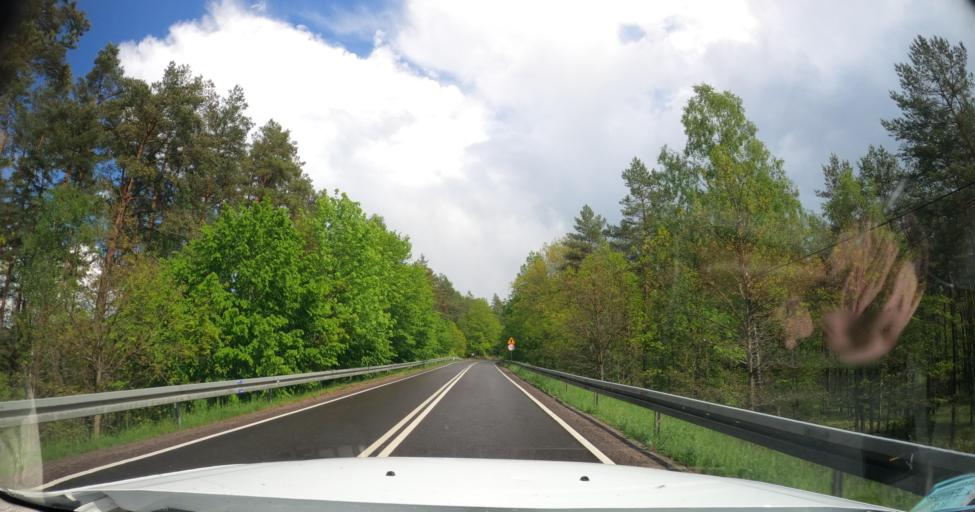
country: PL
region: Pomeranian Voivodeship
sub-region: Powiat bytowski
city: Czarna Dabrowka
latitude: 54.3392
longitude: 17.6316
